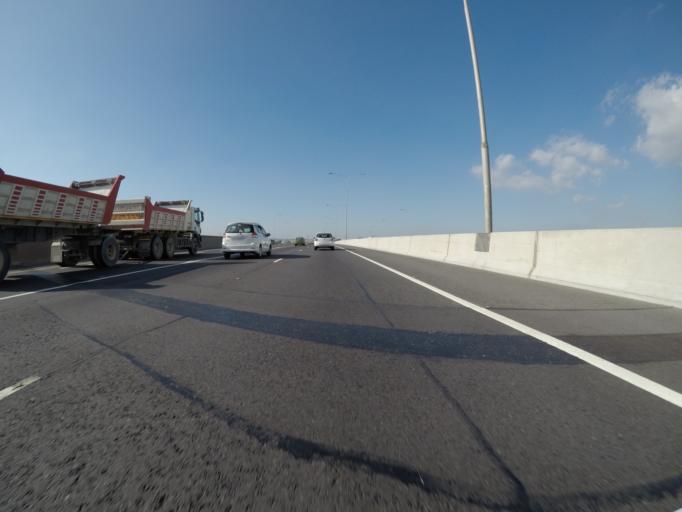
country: ZA
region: Western Cape
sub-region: City of Cape Town
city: Kraaifontein
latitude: -33.9191
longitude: 18.6657
